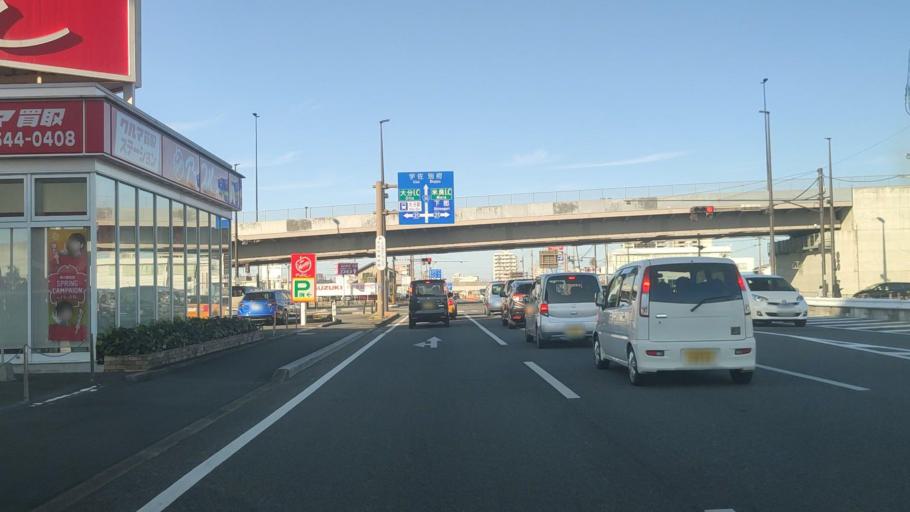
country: JP
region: Oita
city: Oita
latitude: 33.2255
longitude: 131.6187
